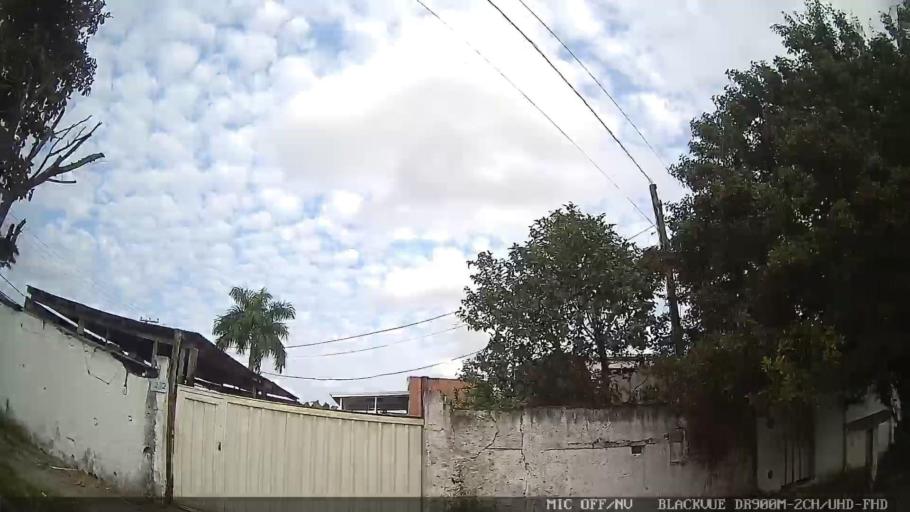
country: BR
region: Sao Paulo
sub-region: Guaruja
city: Guaruja
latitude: -23.9598
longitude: -46.2839
